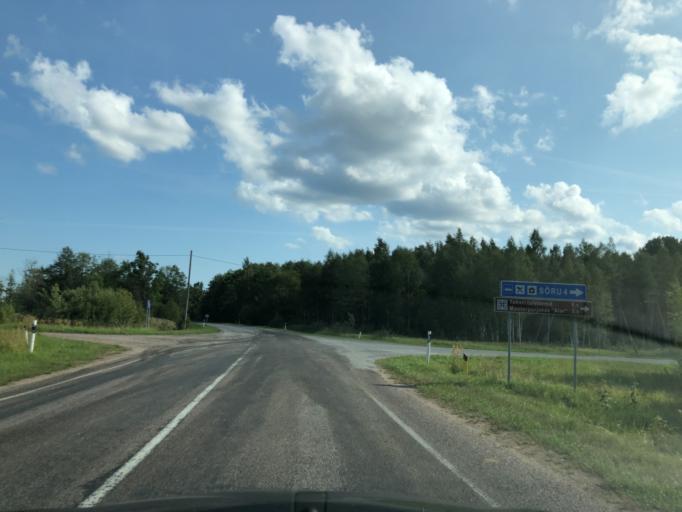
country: EE
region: Hiiumaa
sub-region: Kaerdla linn
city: Kardla
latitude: 58.7198
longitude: 22.5639
